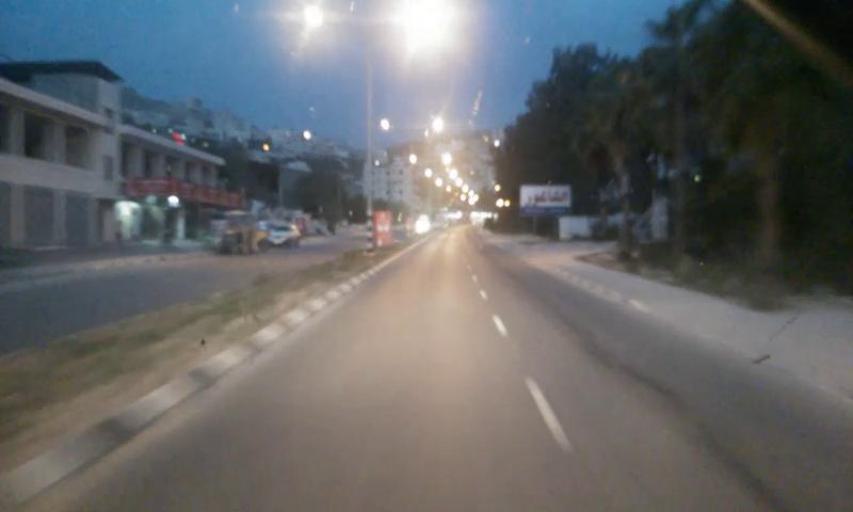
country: PS
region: West Bank
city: Zawata
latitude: 32.2417
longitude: 35.2245
